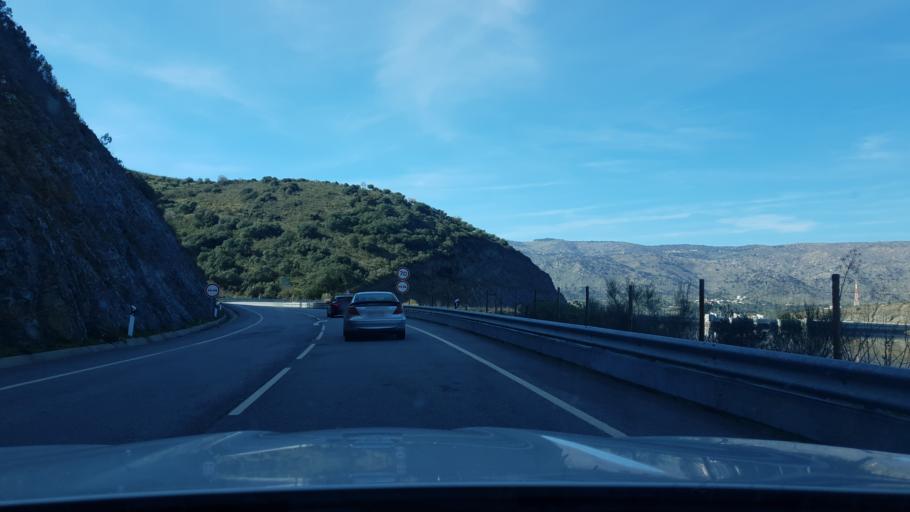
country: PT
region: Braganca
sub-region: Torre de Moncorvo
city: Torre de Moncorvo
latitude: 41.2020
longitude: -7.0854
